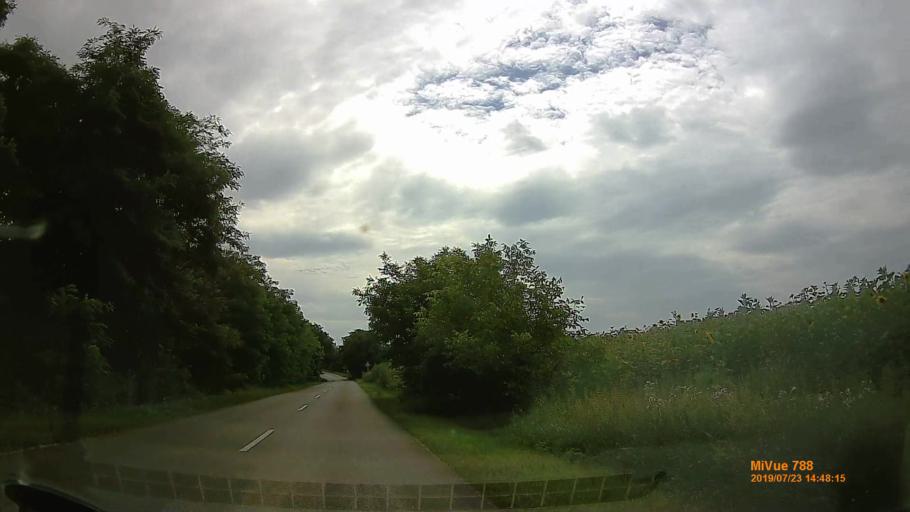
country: HU
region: Szabolcs-Szatmar-Bereg
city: Nyiregyhaza
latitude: 47.9048
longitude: 21.6707
